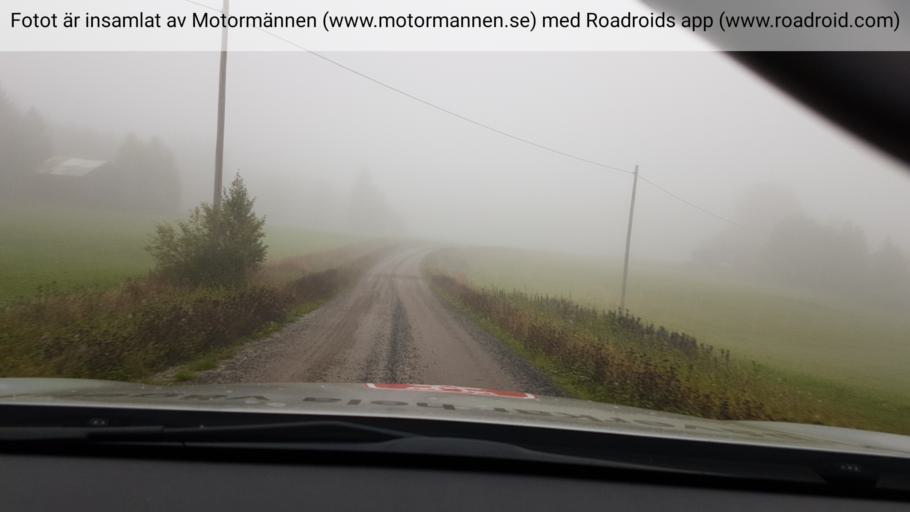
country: SE
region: Vaesterbotten
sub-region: Skelleftea Kommun
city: Burtraesk
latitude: 64.2961
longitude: 20.4338
